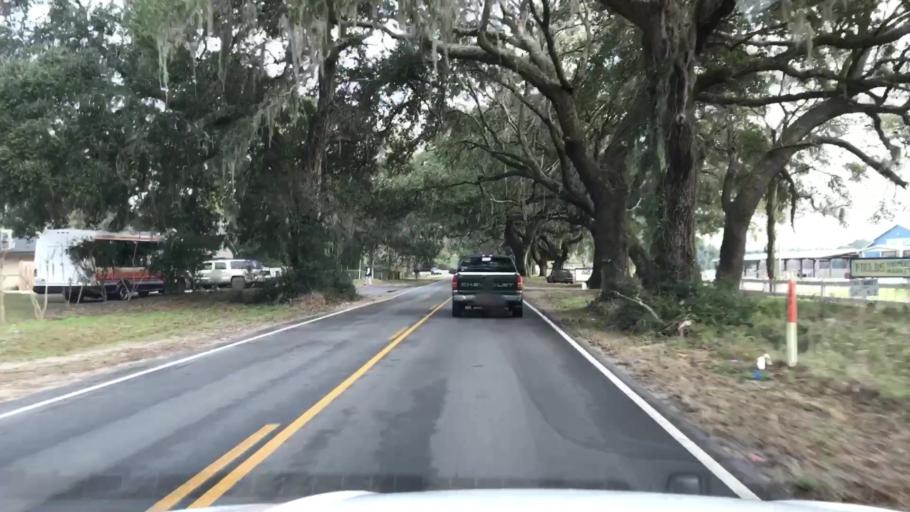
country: US
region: South Carolina
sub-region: Charleston County
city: Folly Beach
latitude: 32.6835
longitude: -80.0243
